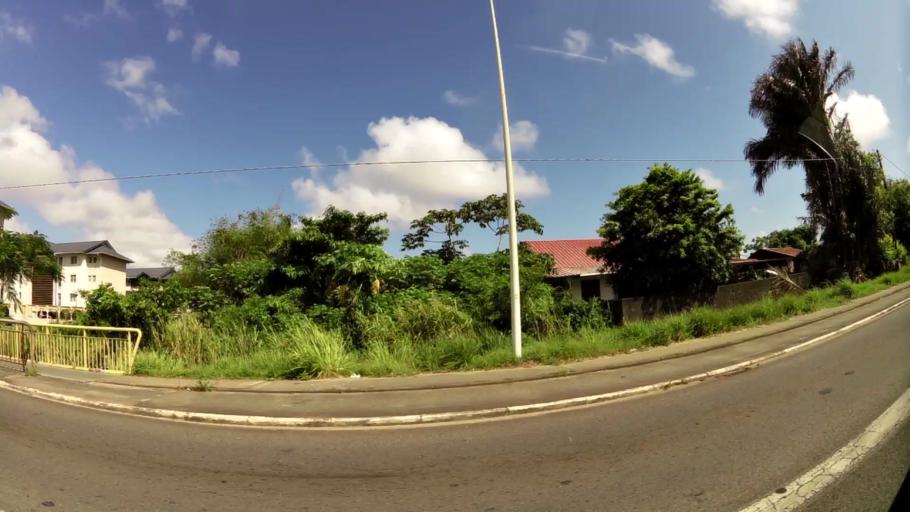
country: GF
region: Guyane
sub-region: Guyane
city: Cayenne
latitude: 4.9353
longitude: -52.3082
